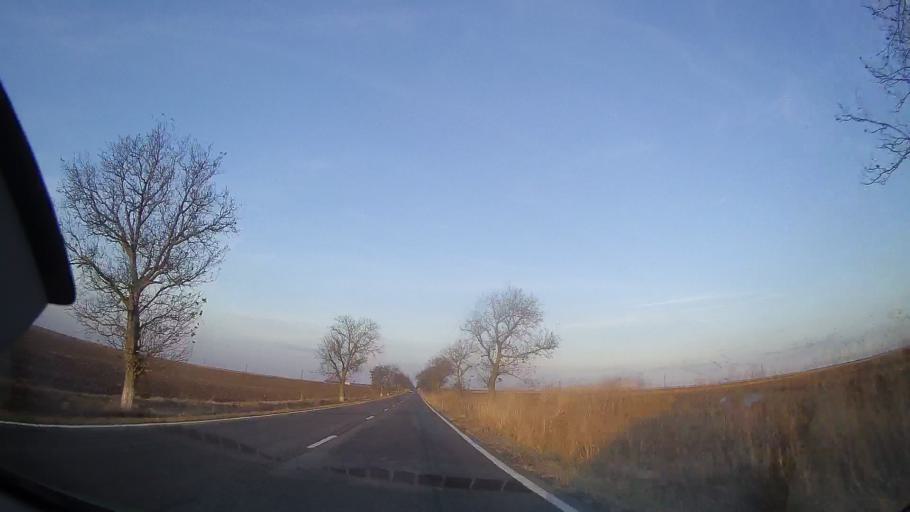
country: RO
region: Constanta
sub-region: Comuna Amzacea
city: Amzacea
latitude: 43.9811
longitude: 28.4156
